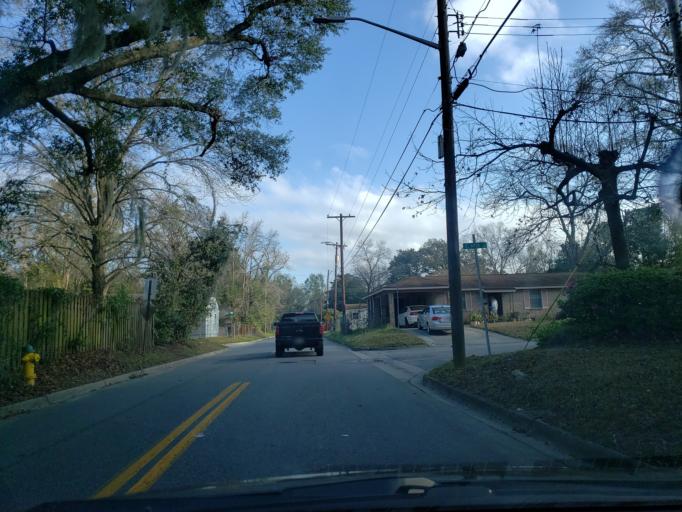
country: US
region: Georgia
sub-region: Chatham County
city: Thunderbolt
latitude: 32.0256
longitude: -81.0903
